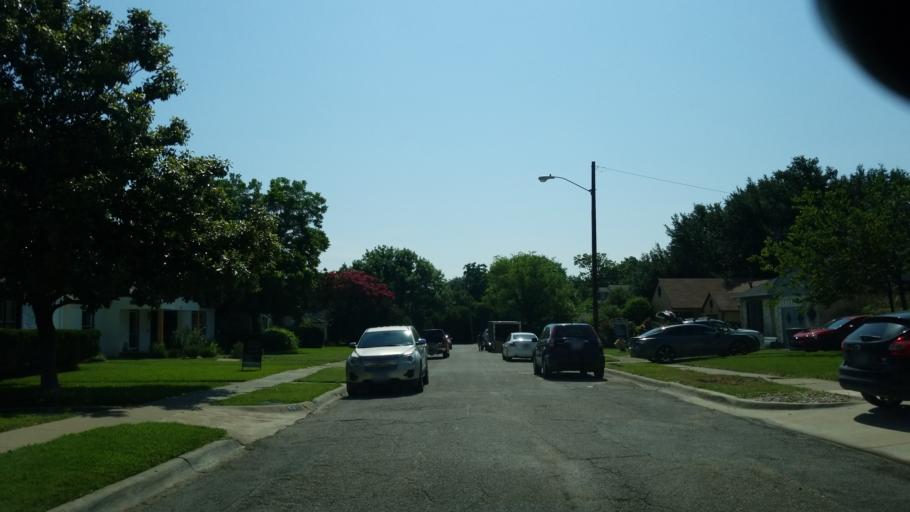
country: US
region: Texas
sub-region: Dallas County
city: Highland Park
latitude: 32.8375
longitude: -96.7673
